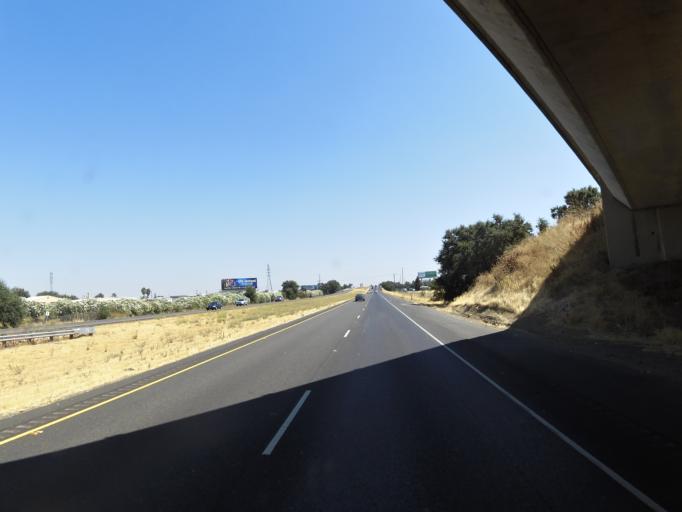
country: US
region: California
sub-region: Yolo County
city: Woodland
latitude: 38.6840
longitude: -121.7508
